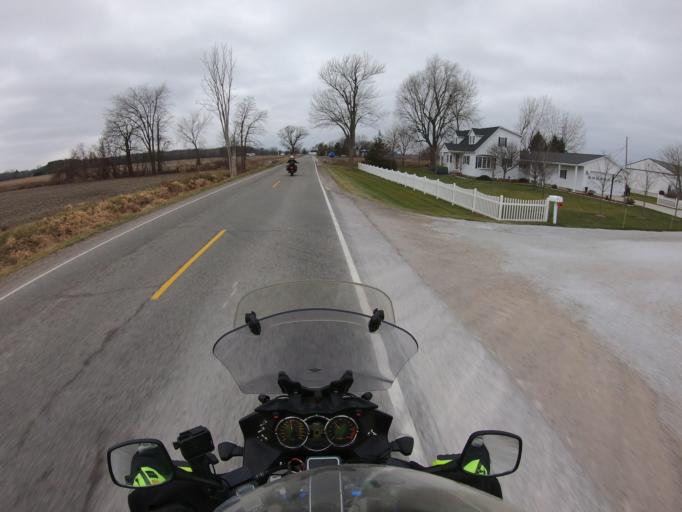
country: US
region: Michigan
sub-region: Saginaw County
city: Saint Charles
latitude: 43.2556
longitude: -84.0650
